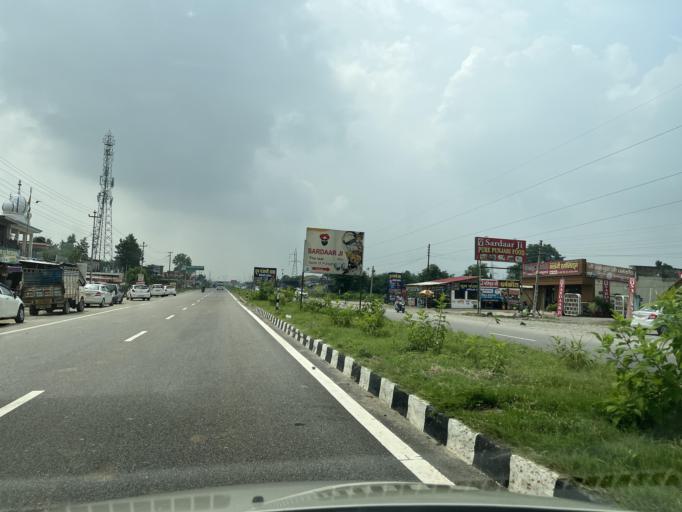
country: IN
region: Uttarakhand
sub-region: Dehradun
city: Raiwala
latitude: 30.0890
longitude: 78.1859
